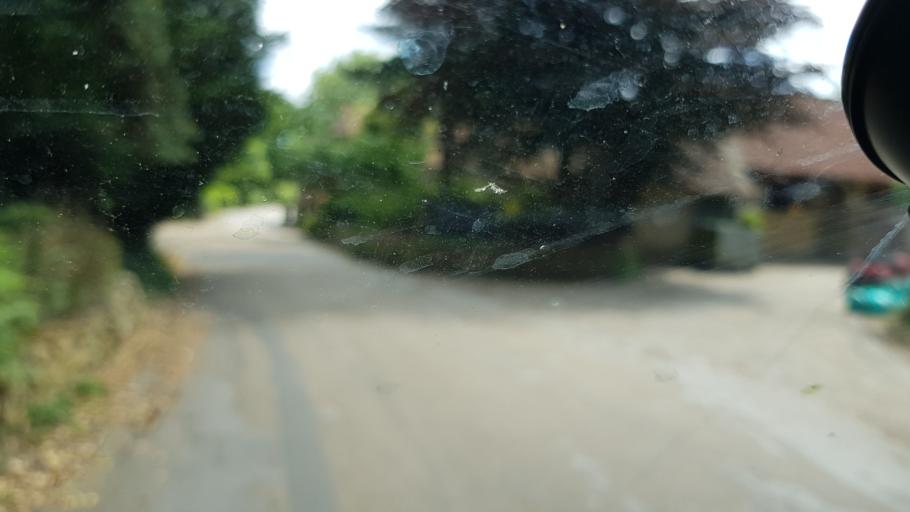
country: GB
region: England
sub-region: West Sussex
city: East Grinstead
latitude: 51.1036
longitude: -0.0175
